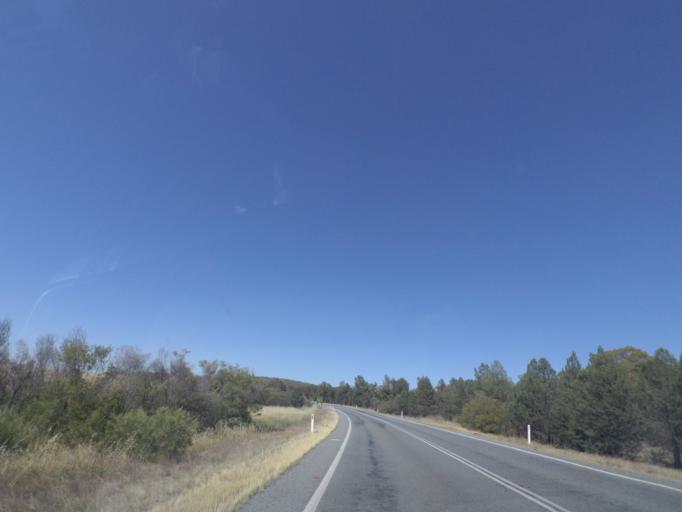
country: AU
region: New South Wales
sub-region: Narrandera
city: Narrandera
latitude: -34.4197
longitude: 146.8470
